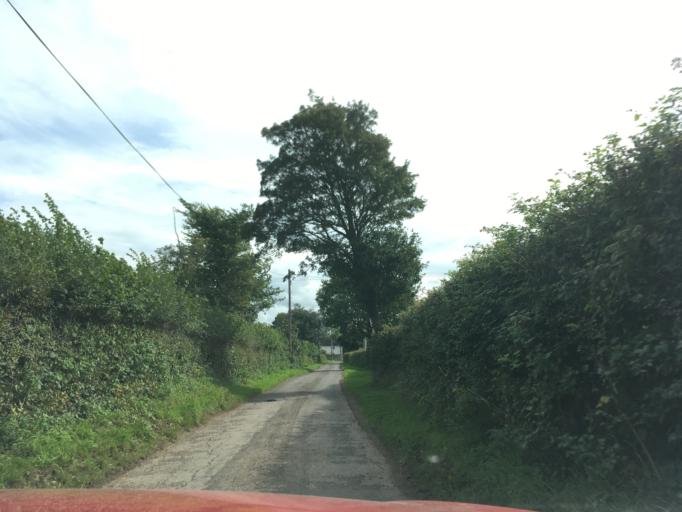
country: GB
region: England
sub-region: South Gloucestershire
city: Falfield
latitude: 51.6080
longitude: -2.4440
